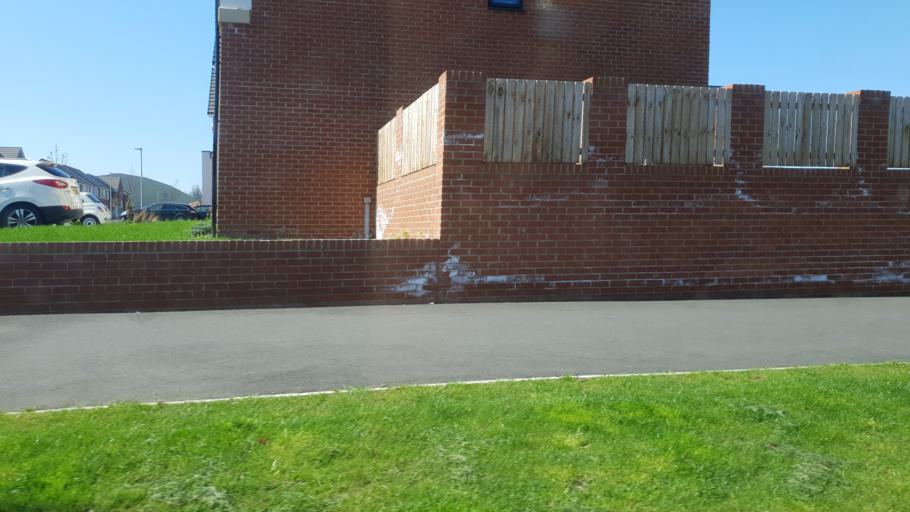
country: GB
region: England
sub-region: Middlesbrough
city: Nunthorpe
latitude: 54.5435
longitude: -1.2068
